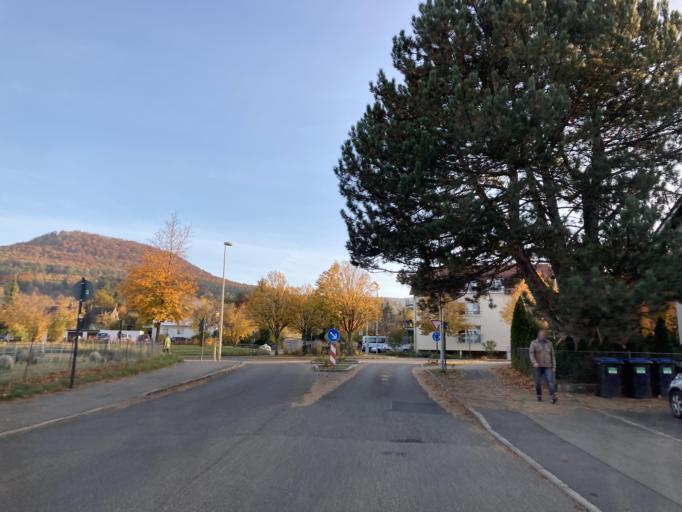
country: DE
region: Baden-Wuerttemberg
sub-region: Tuebingen Region
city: Mossingen
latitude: 48.4021
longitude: 9.0582
